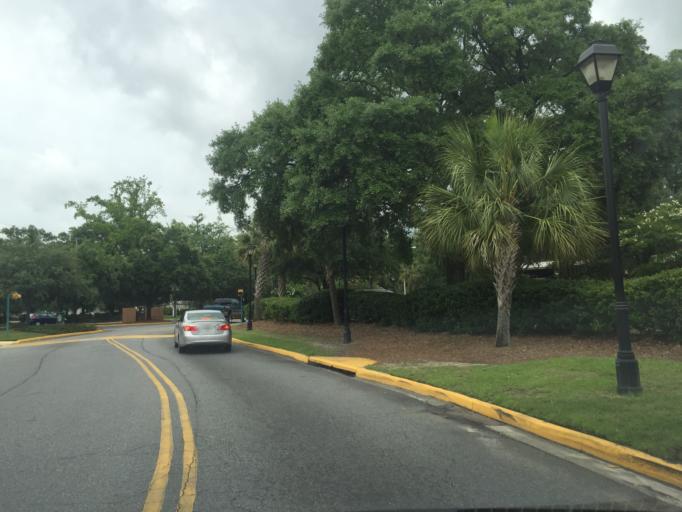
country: US
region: Georgia
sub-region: Chatham County
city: Thunderbolt
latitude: 32.0318
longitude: -81.0912
